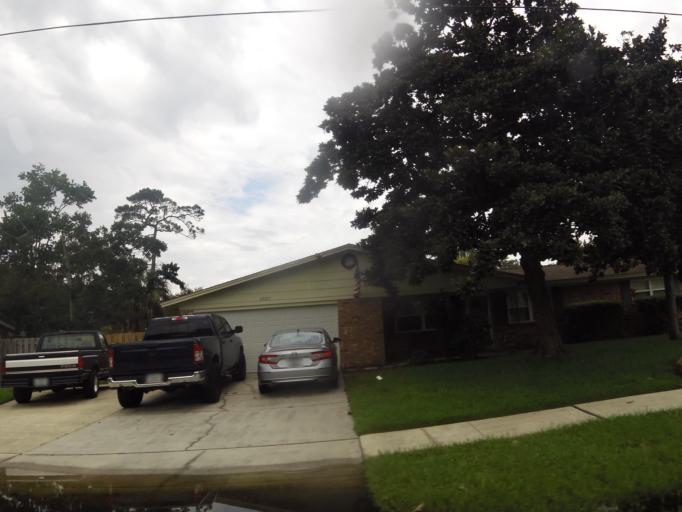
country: US
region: Florida
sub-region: Duval County
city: Jacksonville Beach
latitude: 30.2754
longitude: -81.4337
